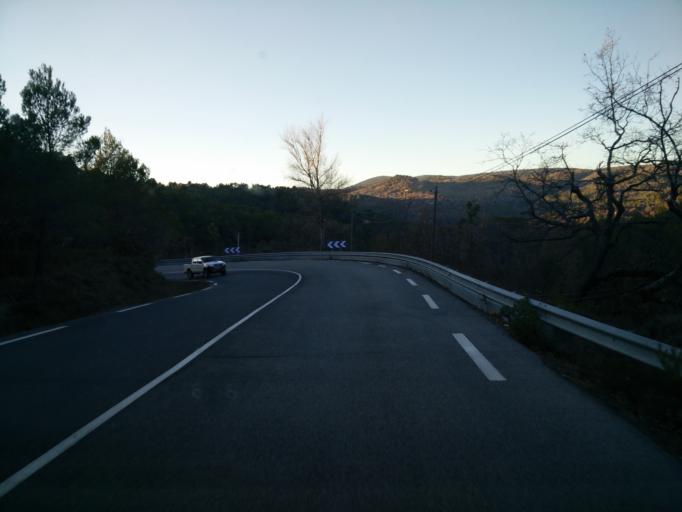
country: FR
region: Provence-Alpes-Cote d'Azur
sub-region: Departement du Var
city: Montferrat
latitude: 43.5890
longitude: 6.4736
